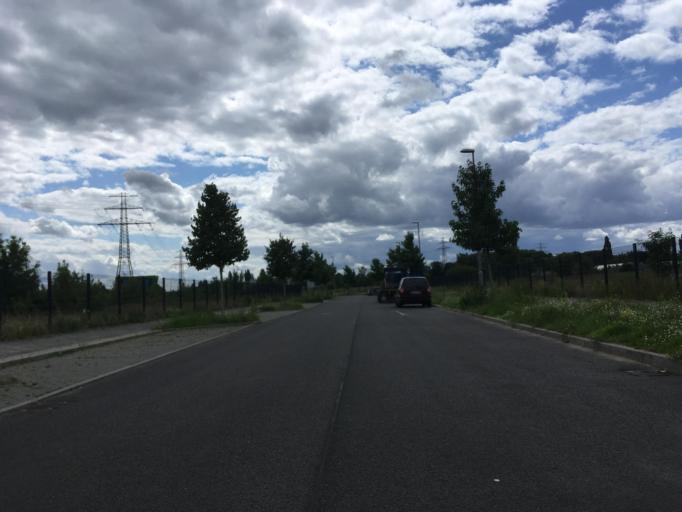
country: DE
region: Berlin
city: Falkenberg
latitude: 52.5568
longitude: 13.5381
